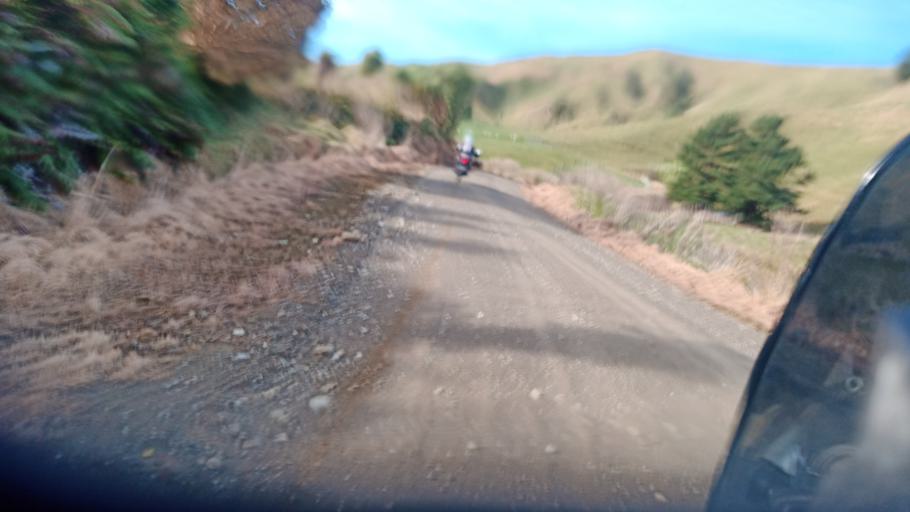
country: NZ
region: Bay of Plenty
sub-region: Opotiki District
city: Opotiki
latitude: -38.4463
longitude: 177.5380
